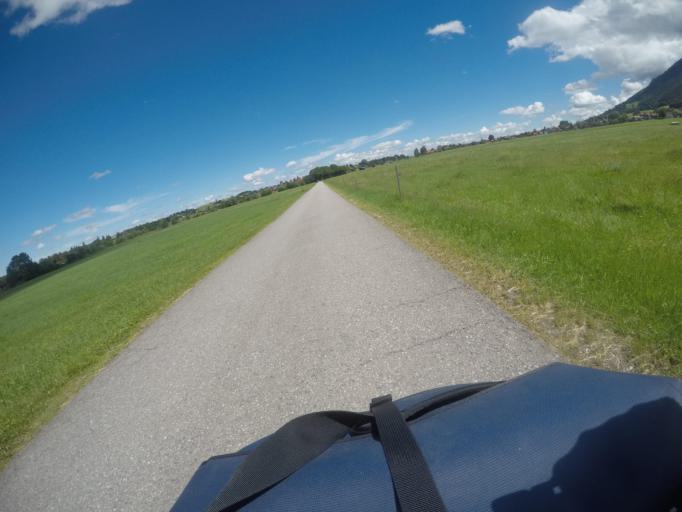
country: DE
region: Bavaria
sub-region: Swabia
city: Halblech
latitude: 47.6153
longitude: 10.7988
